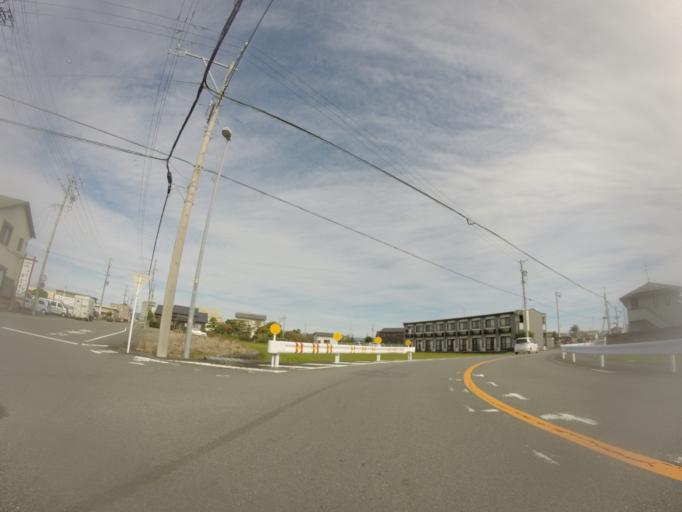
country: JP
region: Shizuoka
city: Shimada
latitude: 34.7894
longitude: 138.2399
